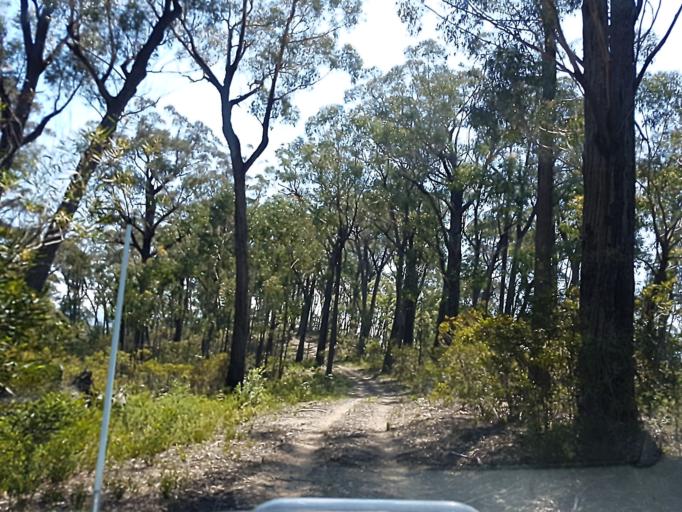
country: AU
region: Victoria
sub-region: East Gippsland
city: Lakes Entrance
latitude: -37.3139
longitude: 148.3429
